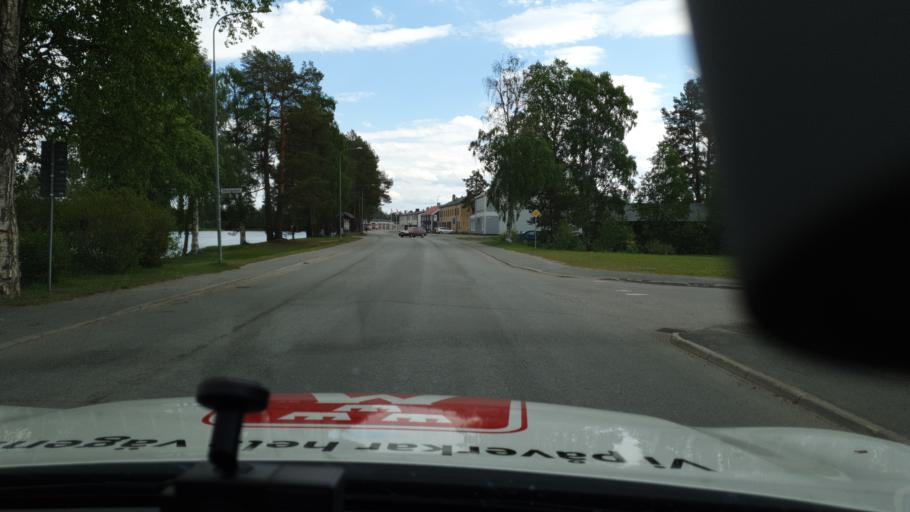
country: SE
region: Vaesterbotten
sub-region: Sorsele Kommun
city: Sorsele
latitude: 65.5390
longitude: 17.5234
